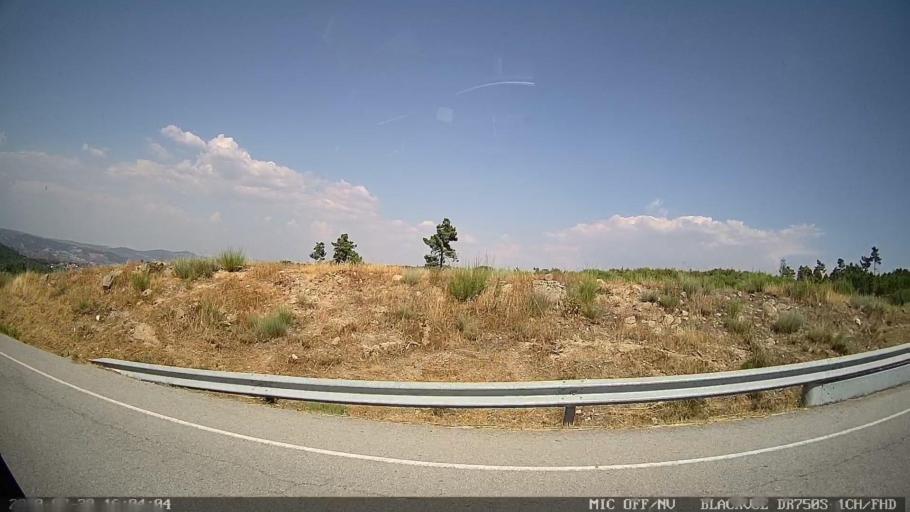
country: PT
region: Vila Real
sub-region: Murca
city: Murca
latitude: 41.3542
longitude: -7.4856
